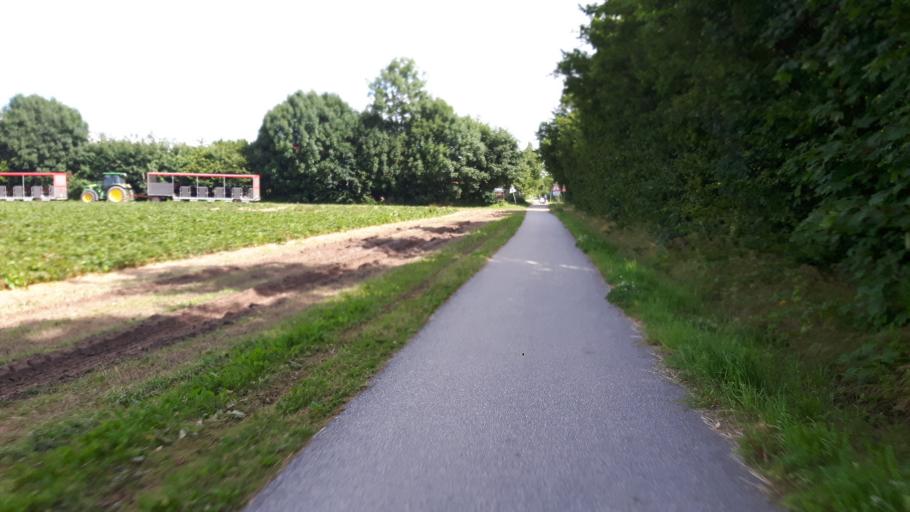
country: DE
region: Schleswig-Holstein
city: Travemuende
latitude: 53.9469
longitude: 10.8513
